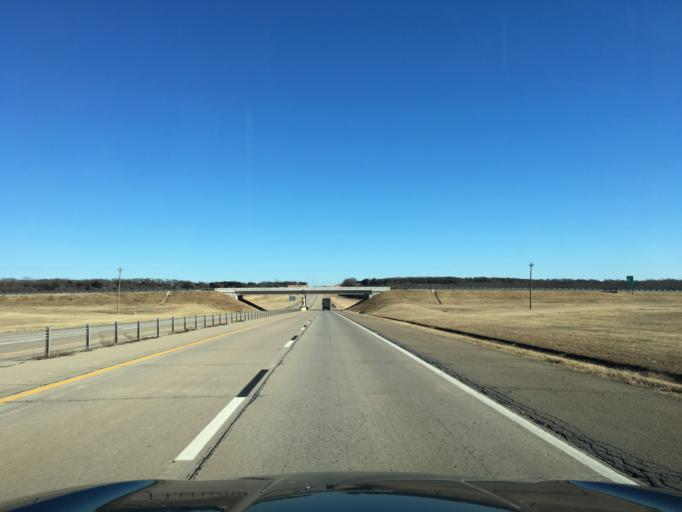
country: US
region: Oklahoma
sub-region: Pawnee County
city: Pawnee
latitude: 36.2248
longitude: -96.7869
